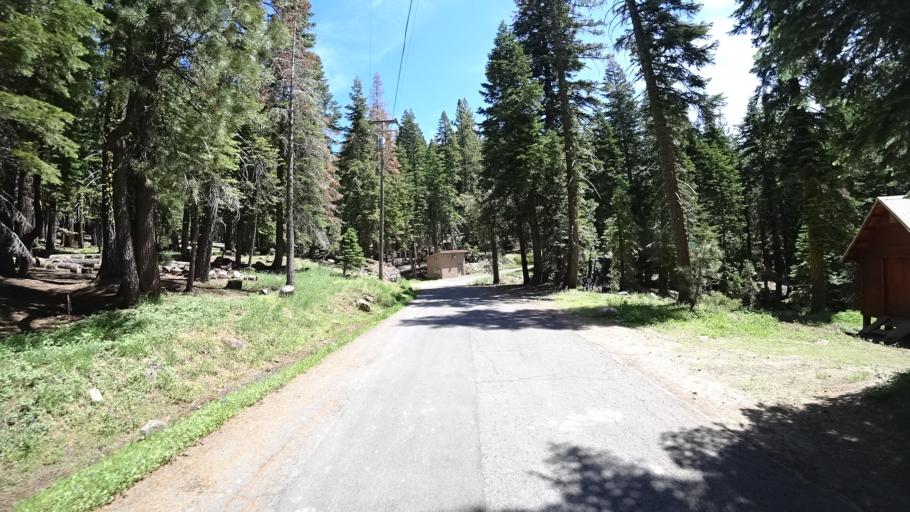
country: US
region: California
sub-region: Calaveras County
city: Arnold
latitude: 38.4297
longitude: -120.1002
